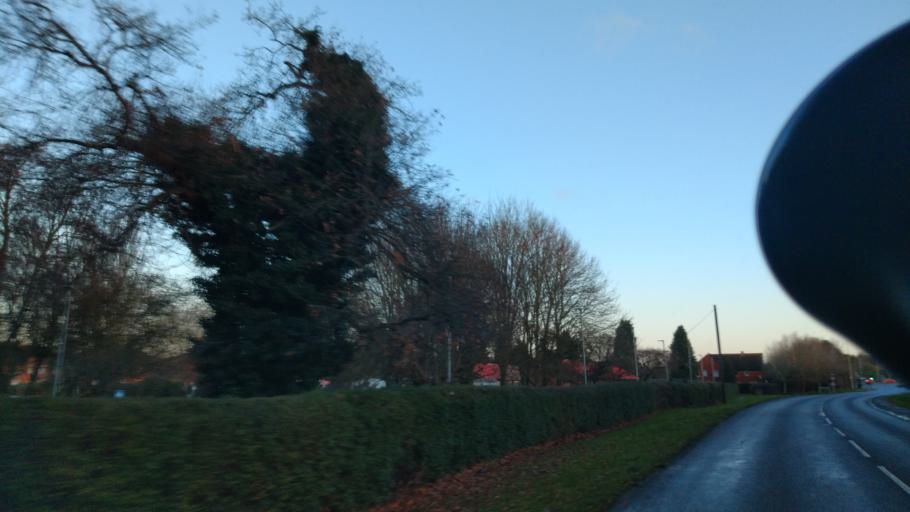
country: GB
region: England
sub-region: Oxfordshire
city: Shrivenham
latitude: 51.6117
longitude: -1.6381
